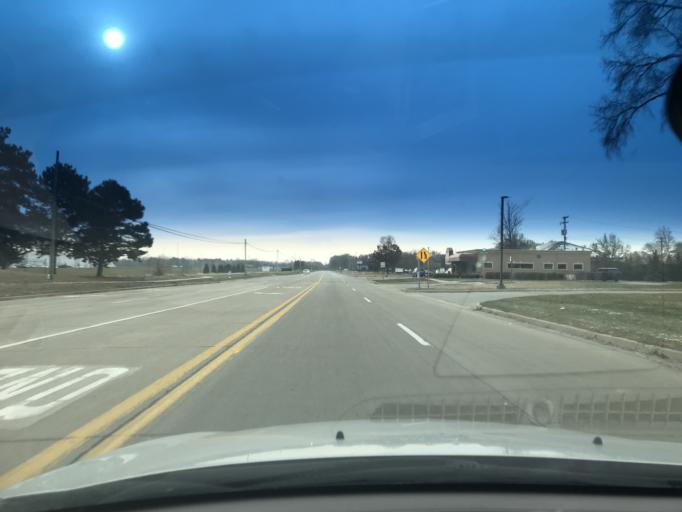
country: US
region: Michigan
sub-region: Macomb County
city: Shelby
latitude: 42.6689
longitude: -83.0536
